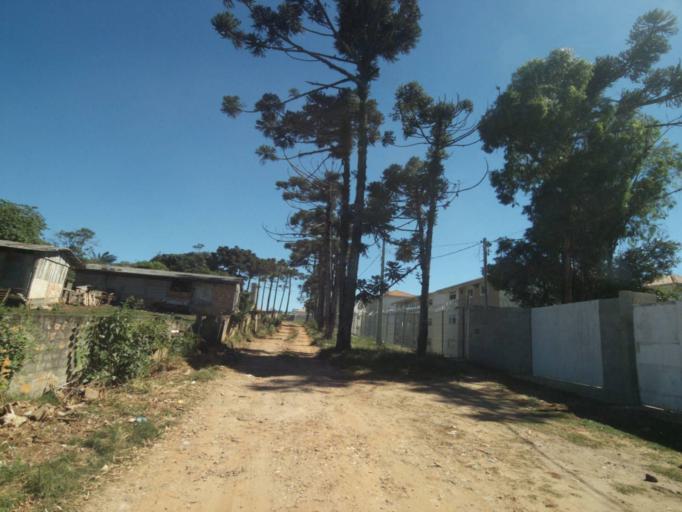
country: BR
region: Parana
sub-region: Curitiba
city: Curitiba
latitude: -25.4888
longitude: -49.3397
